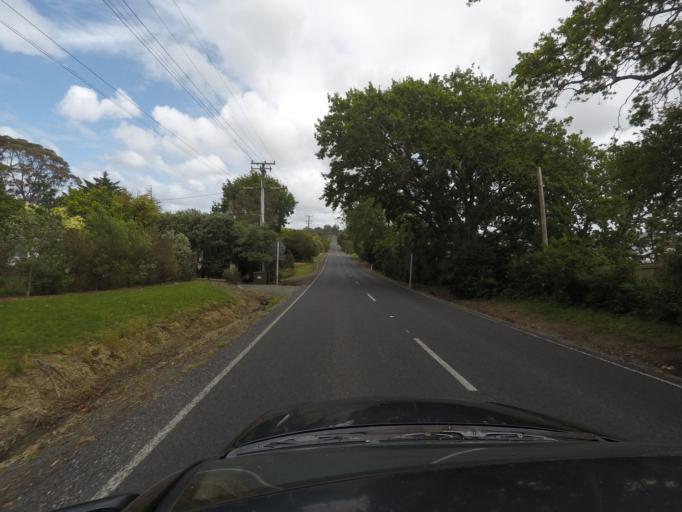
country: NZ
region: Auckland
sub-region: Auckland
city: Parakai
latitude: -36.6281
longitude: 174.5022
